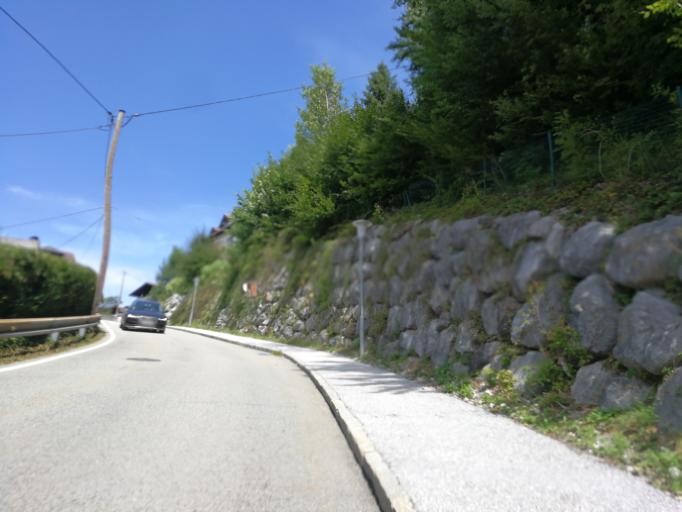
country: AT
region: Salzburg
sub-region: Politischer Bezirk Salzburg-Umgebung
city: Hallwang
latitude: 47.8412
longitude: 13.0662
